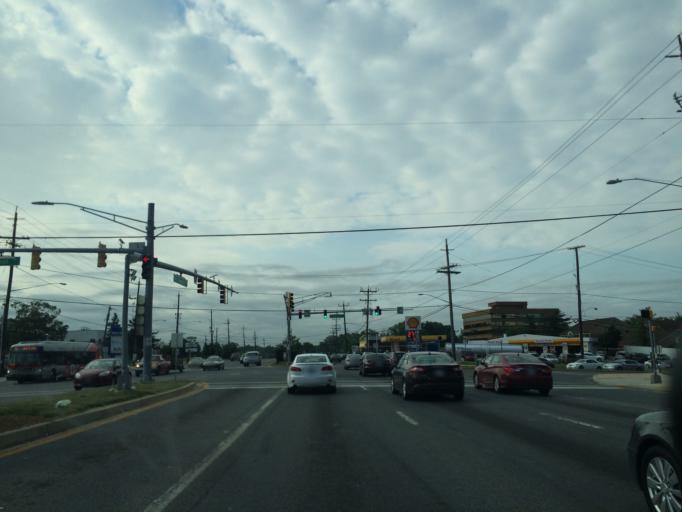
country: US
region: Maryland
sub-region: Montgomery County
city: White Oak
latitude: 39.0402
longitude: -76.9909
